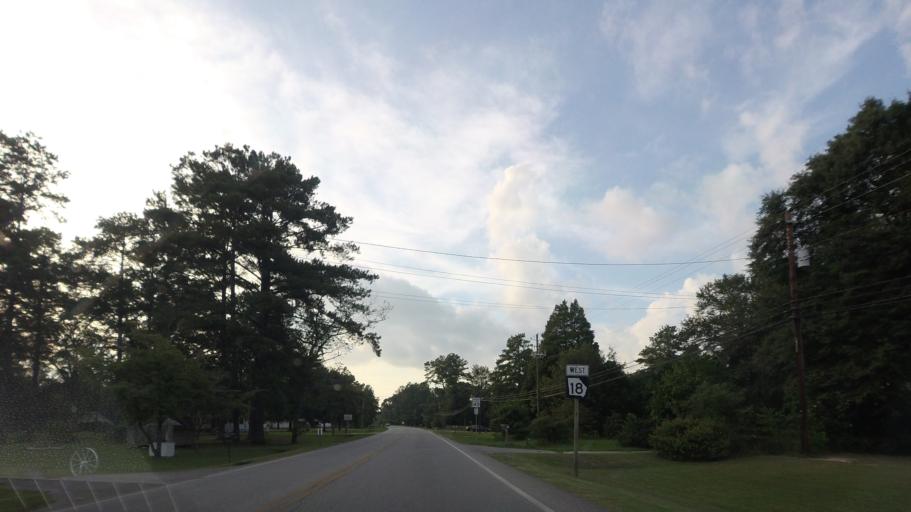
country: US
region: Georgia
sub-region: Wilkinson County
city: Gordon
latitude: 32.8846
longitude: -83.3450
